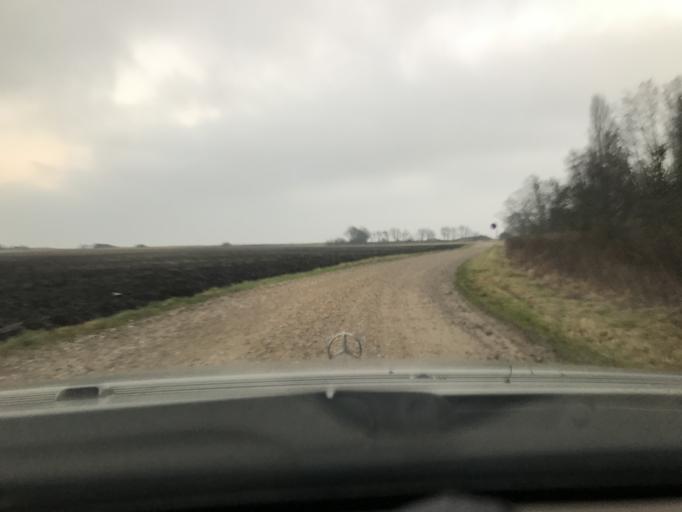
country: DK
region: South Denmark
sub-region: Sonderborg Kommune
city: Horuphav
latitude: 54.8690
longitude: 10.0019
